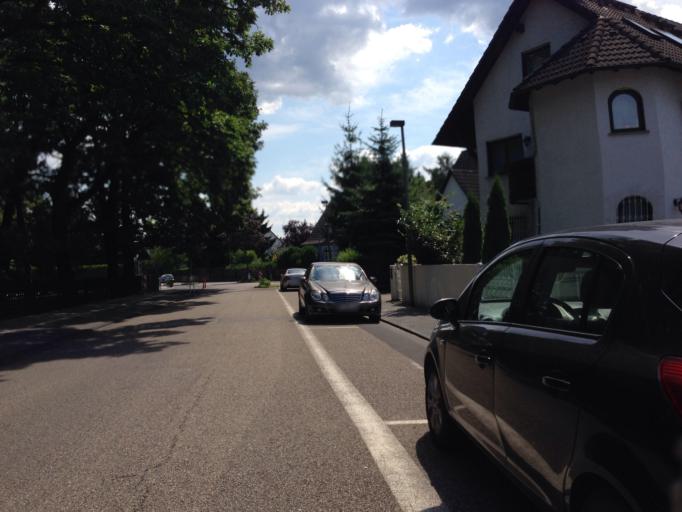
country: DE
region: Hesse
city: Heusenstamm
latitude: 50.0325
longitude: 8.7895
